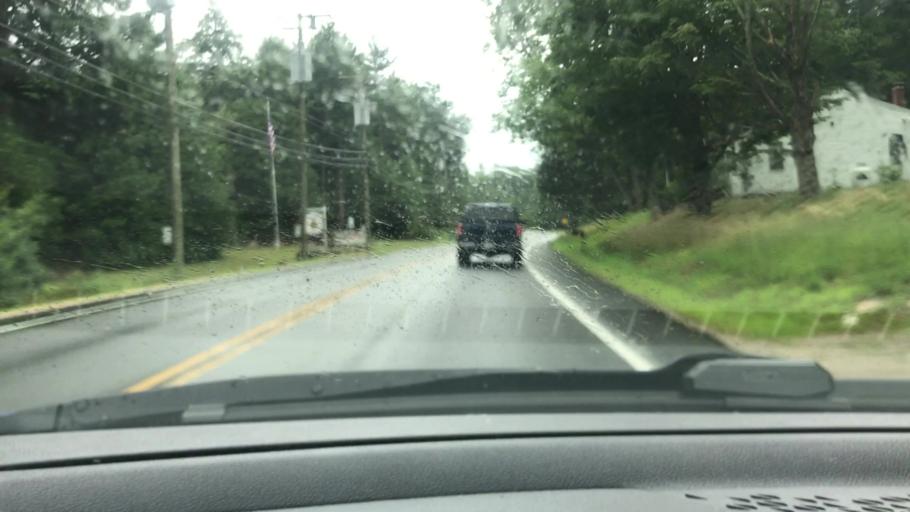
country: US
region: New Hampshire
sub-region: Rockingham County
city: Candia
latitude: 43.1413
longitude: -71.2347
